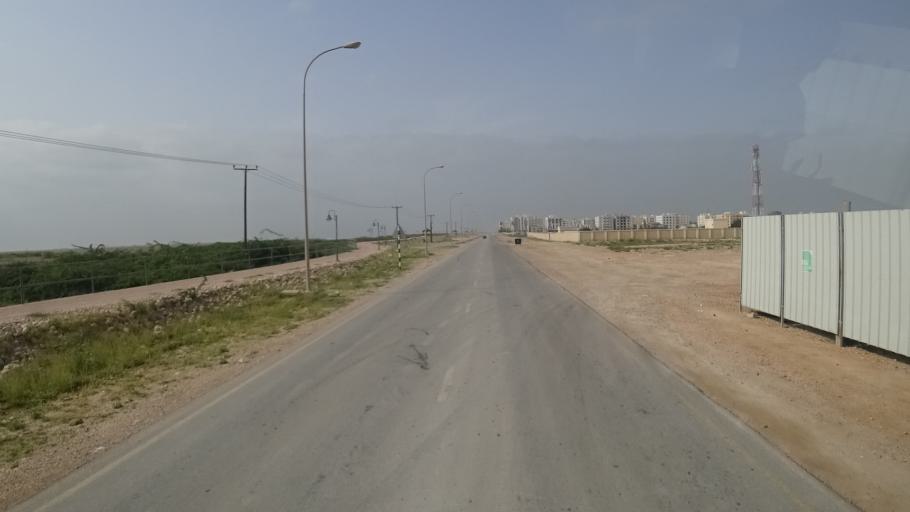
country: OM
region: Zufar
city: Salalah
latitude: 17.0218
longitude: 54.1740
